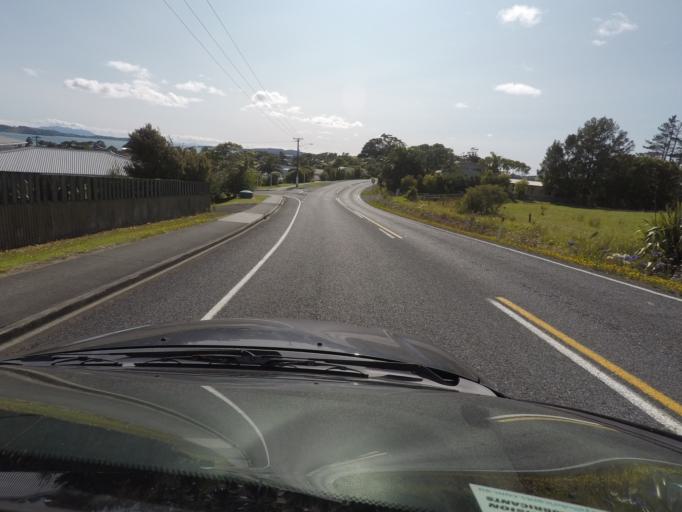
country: NZ
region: Auckland
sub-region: Auckland
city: Warkworth
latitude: -36.4286
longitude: 174.7339
